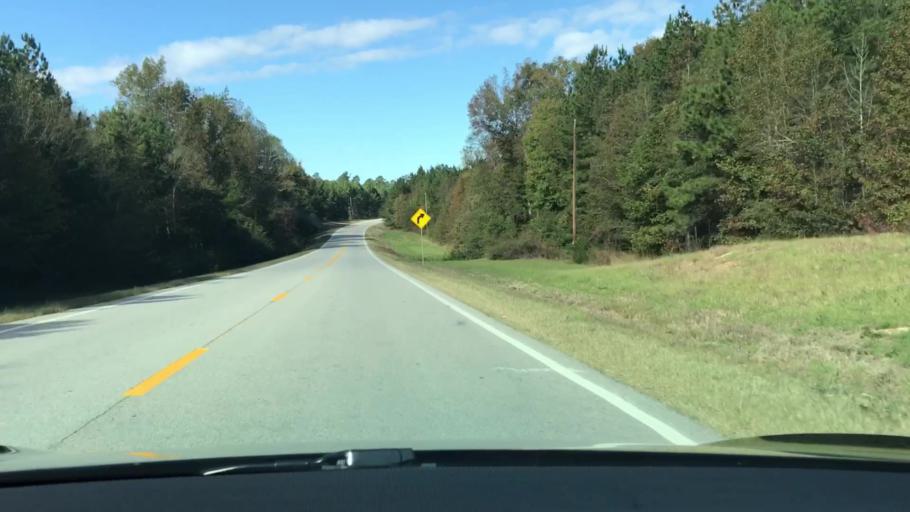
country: US
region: Georgia
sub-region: Jefferson County
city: Wrens
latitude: 33.2641
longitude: -82.4865
